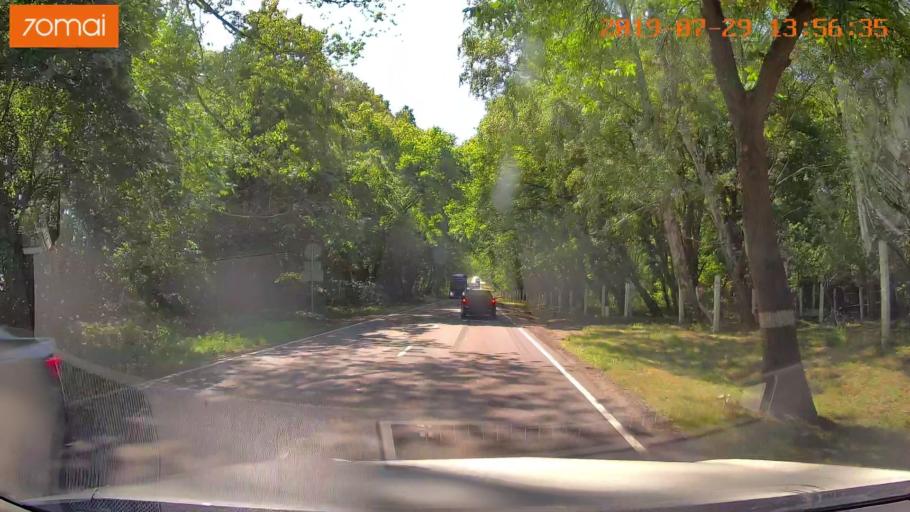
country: RU
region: Kaliningrad
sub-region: Gorod Kaliningrad
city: Baltiysk
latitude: 54.7071
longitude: 19.9480
